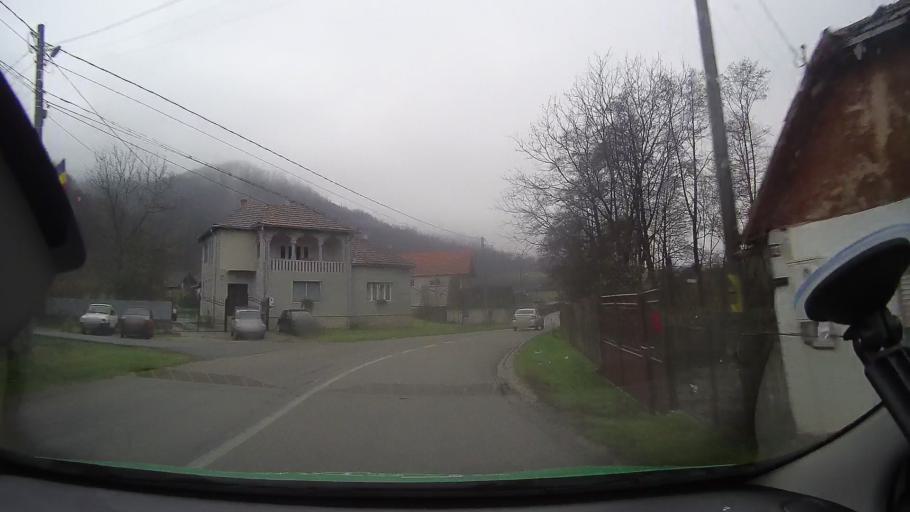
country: RO
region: Arad
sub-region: Comuna Dezna
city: Dezna
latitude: 46.4176
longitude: 22.2558
